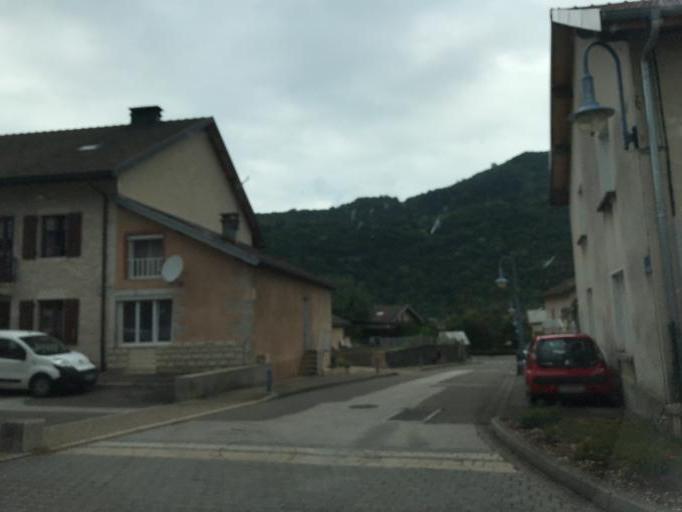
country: FR
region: Franche-Comte
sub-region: Departement du Jura
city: Lavans-les-Saint-Claude
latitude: 46.3559
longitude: 5.7660
